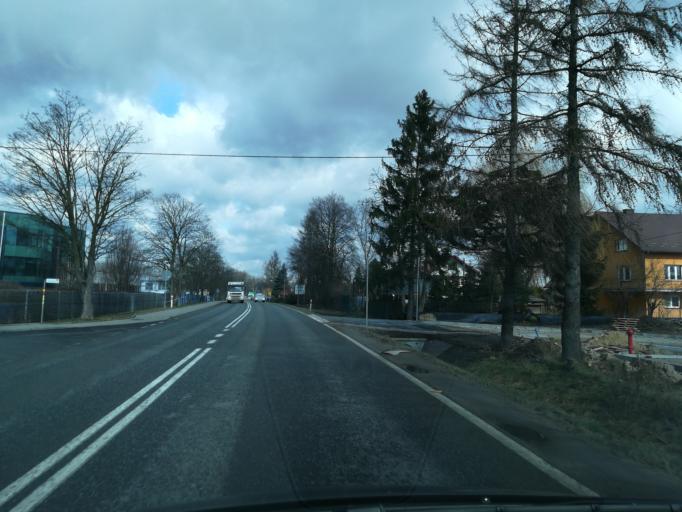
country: PL
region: Lesser Poland Voivodeship
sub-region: Powiat krakowski
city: Kryspinow
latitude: 50.0643
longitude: 19.8034
